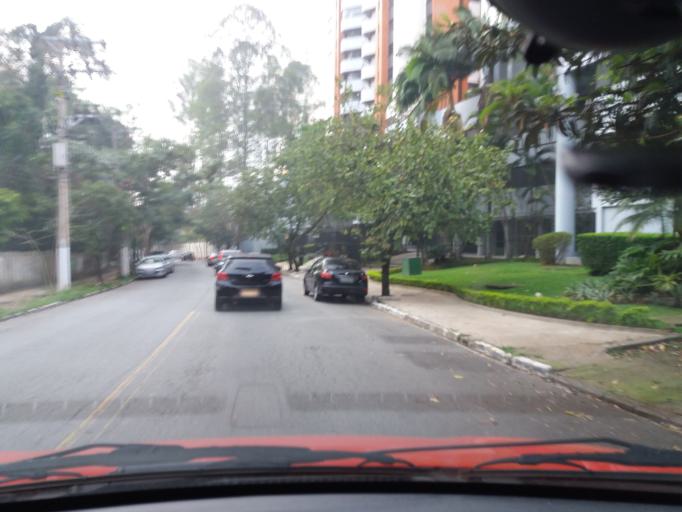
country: BR
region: Sao Paulo
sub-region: Taboao Da Serra
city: Taboao da Serra
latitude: -23.6299
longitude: -46.7311
